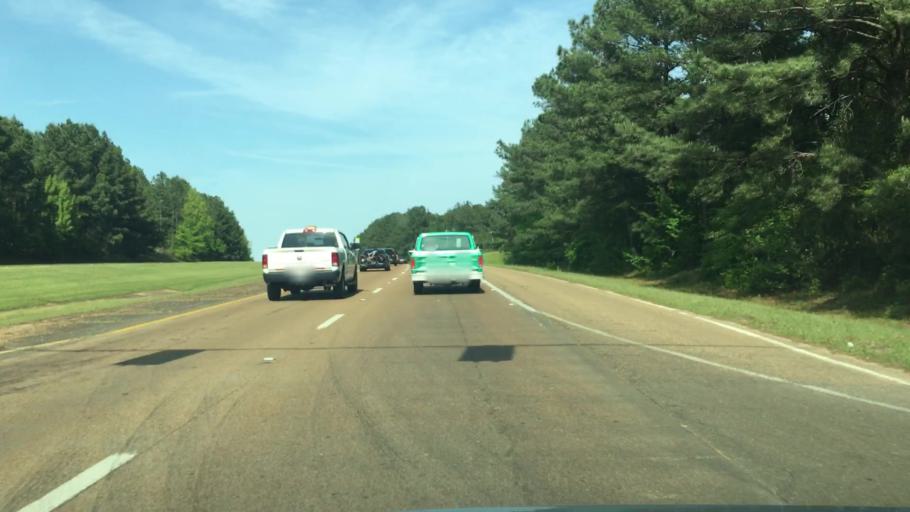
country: US
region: Mississippi
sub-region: Rankin County
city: Brandon
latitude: 32.3620
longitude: -89.9941
